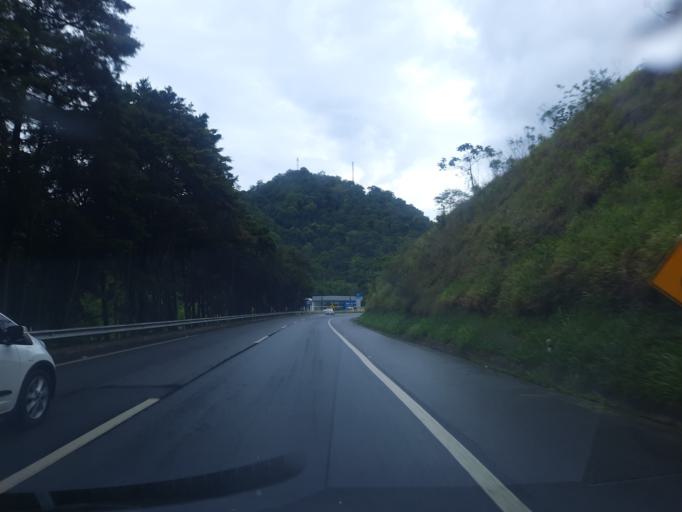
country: BR
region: Rio de Janeiro
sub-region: Petropolis
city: Petropolis
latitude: -22.4226
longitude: -43.1564
